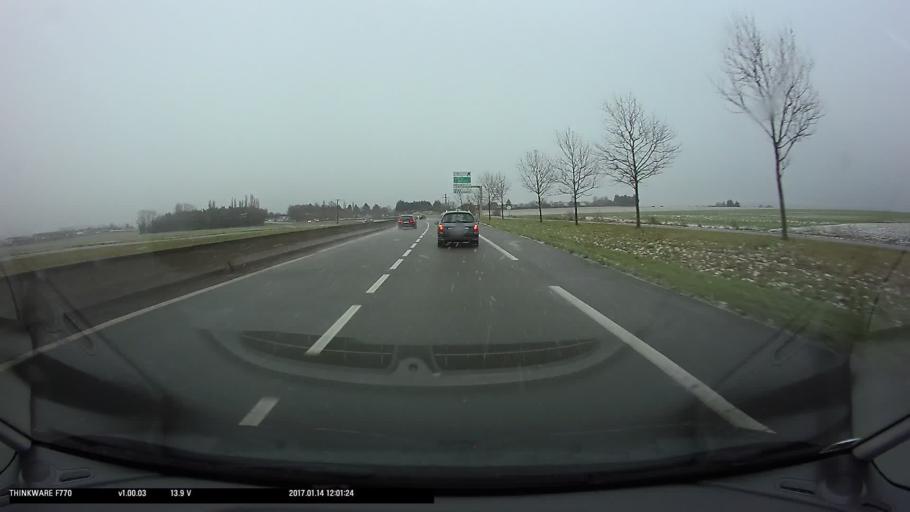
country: FR
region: Ile-de-France
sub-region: Departement du Val-d'Oise
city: Sagy
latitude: 49.0726
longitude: 1.9556
